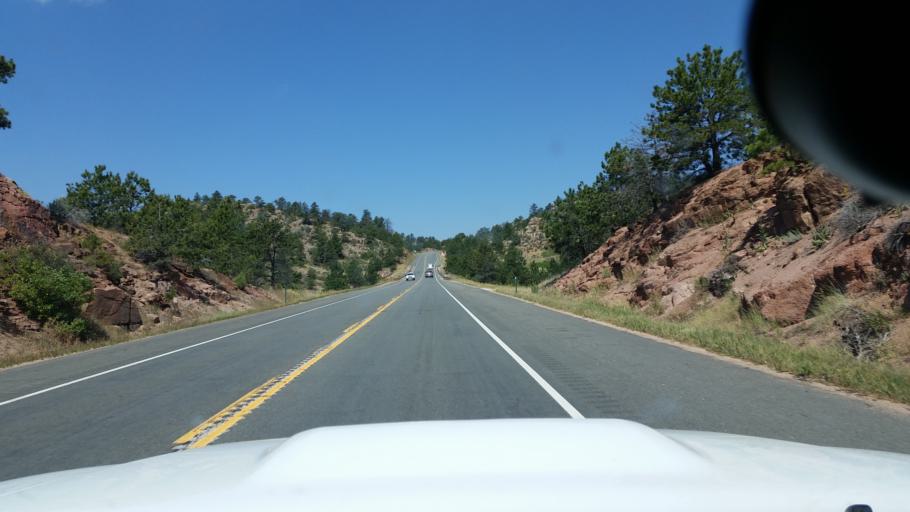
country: US
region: Colorado
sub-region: Larimer County
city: Laporte
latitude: 40.9613
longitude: -105.3650
